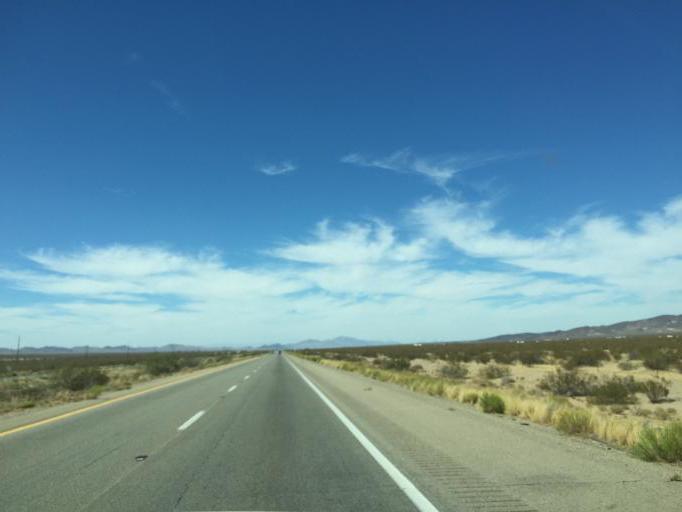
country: US
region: Arizona
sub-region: Mohave County
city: Dolan Springs
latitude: 35.5799
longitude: -114.3870
